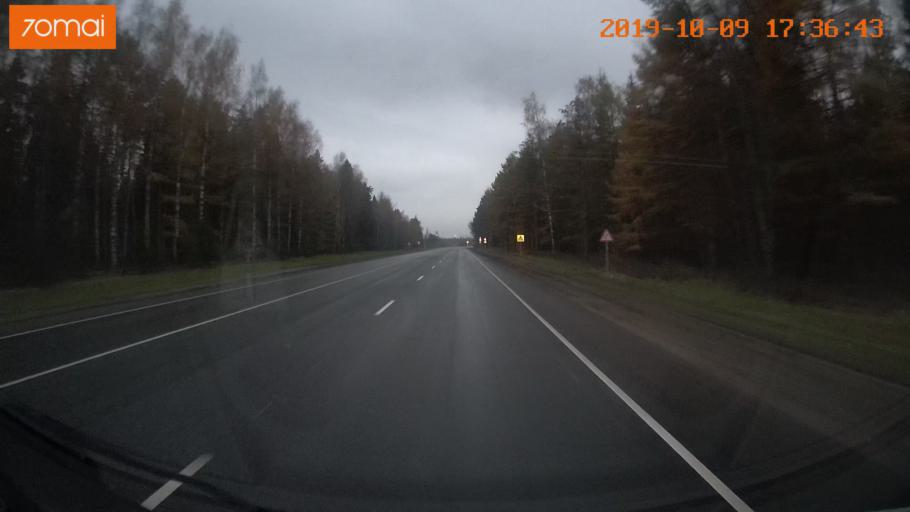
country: RU
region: Ivanovo
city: Bogorodskoye
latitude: 57.0745
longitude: 40.9934
